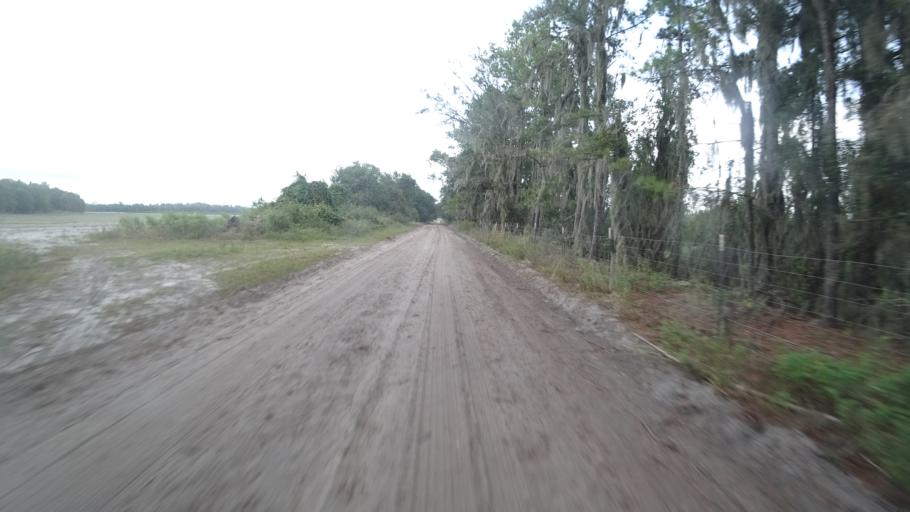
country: US
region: Florida
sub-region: Hillsborough County
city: Wimauma
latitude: 27.6076
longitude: -82.1329
